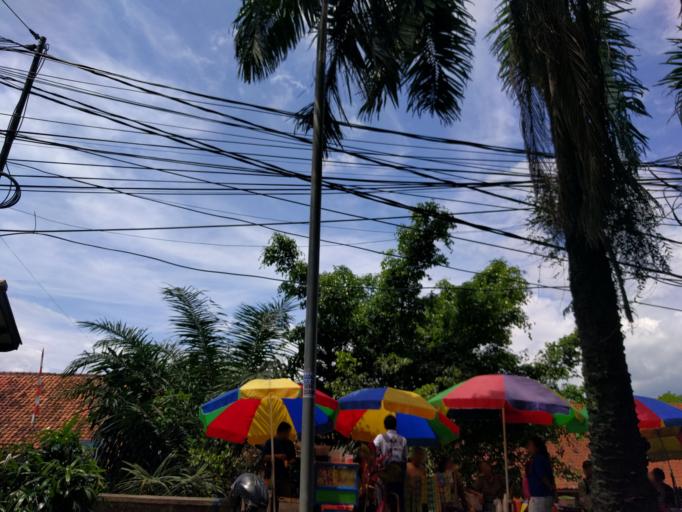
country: ID
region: West Java
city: Bogor
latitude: -6.6018
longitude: 106.8039
